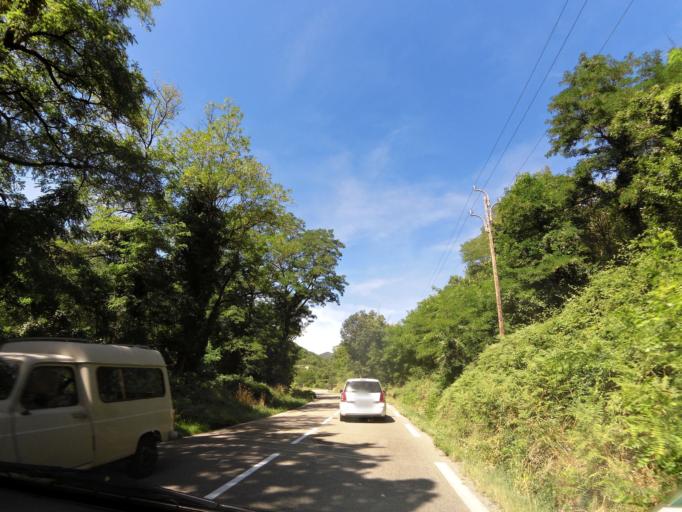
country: FR
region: Languedoc-Roussillon
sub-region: Departement du Gard
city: Le Vigan
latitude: 43.9759
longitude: 3.5051
